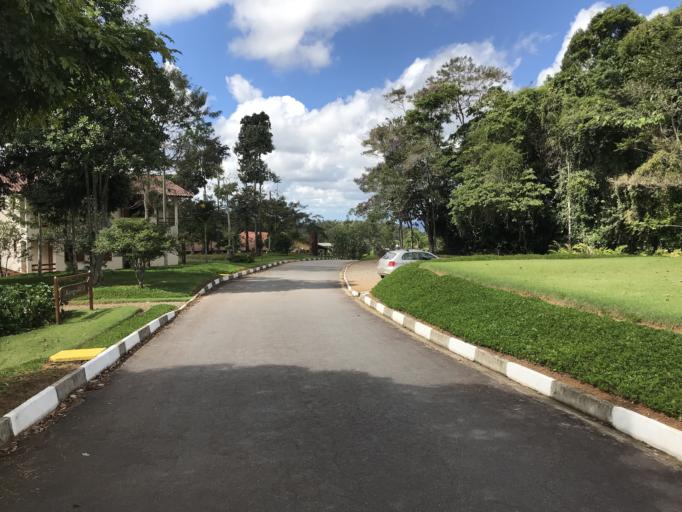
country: BR
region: Bahia
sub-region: Gandu
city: Gandu
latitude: -13.8979
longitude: -39.4584
